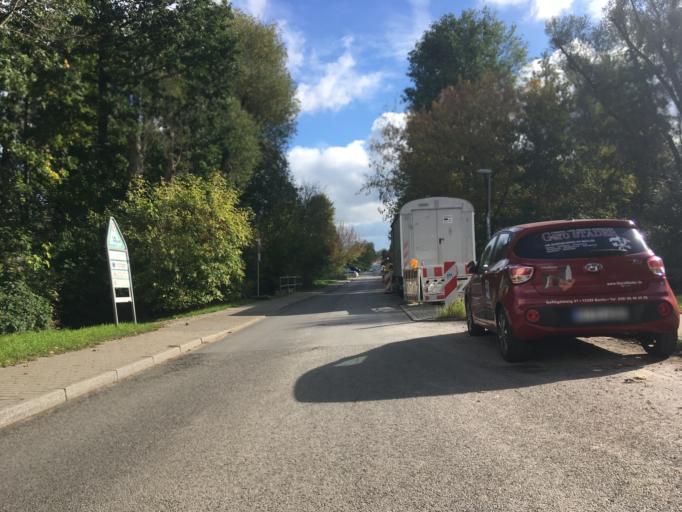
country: DE
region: Berlin
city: Rudow
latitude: 52.4077
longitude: 13.4832
